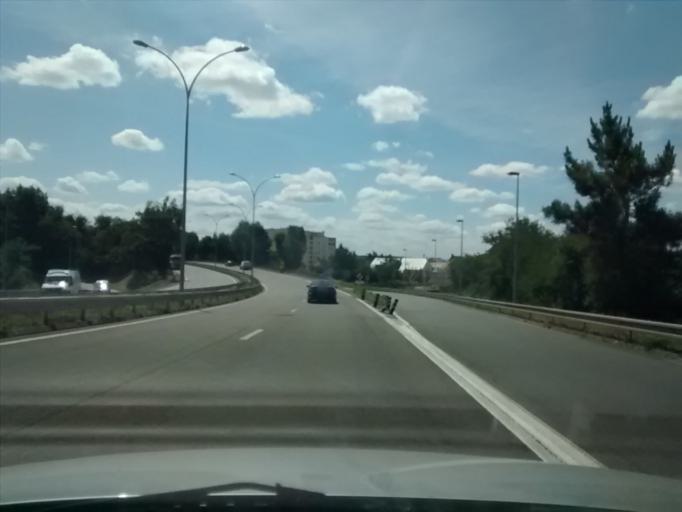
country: FR
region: Pays de la Loire
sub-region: Departement de la Sarthe
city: Le Mans
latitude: 47.9949
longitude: 0.1724
